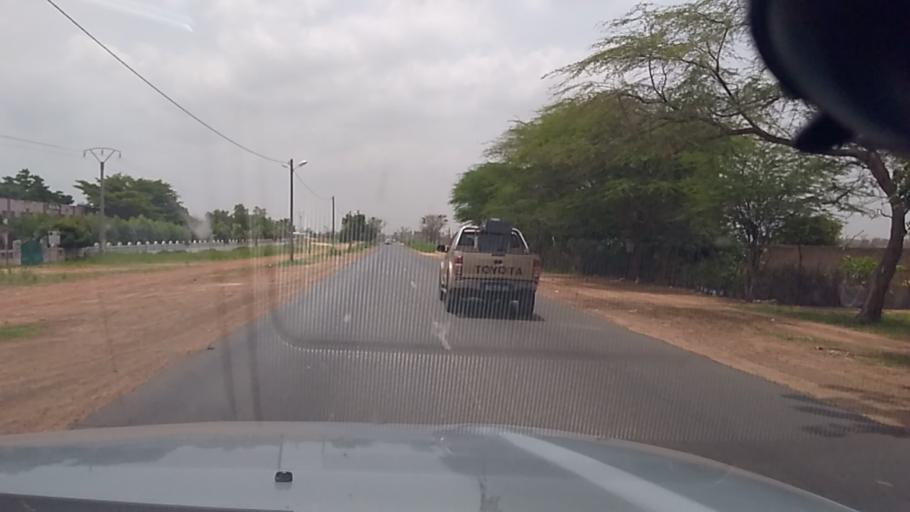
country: SN
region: Thies
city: Mekhe
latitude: 15.0099
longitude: -16.7422
